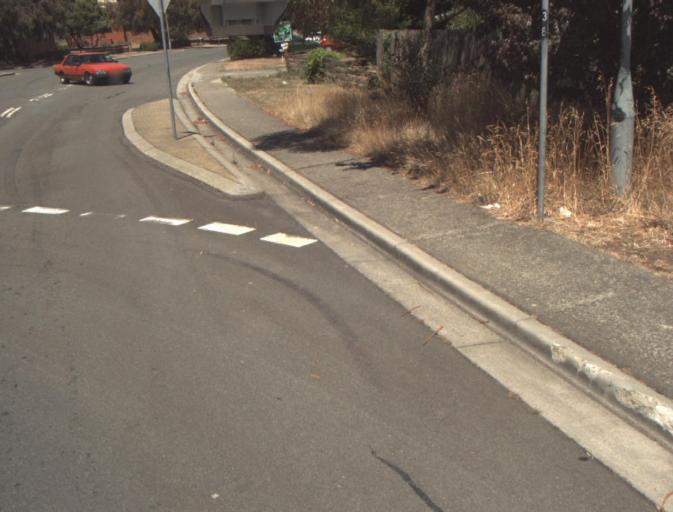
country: AU
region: Tasmania
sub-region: Launceston
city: Mayfield
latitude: -41.3780
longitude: 147.1353
